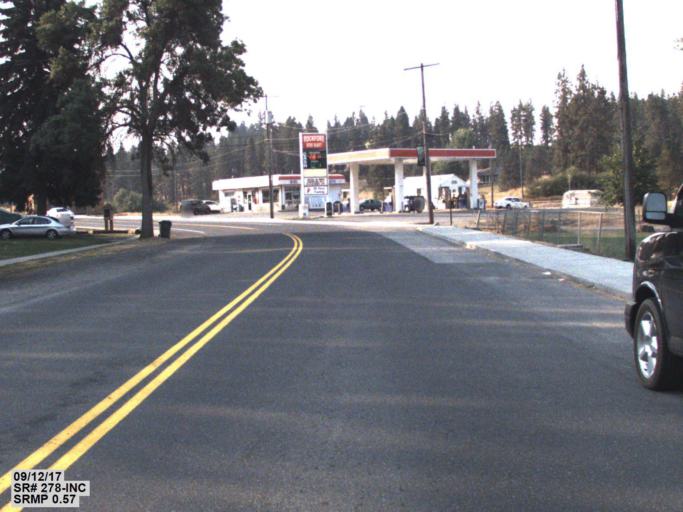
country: US
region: Washington
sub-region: Spokane County
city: Veradale
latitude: 47.4512
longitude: -117.1320
